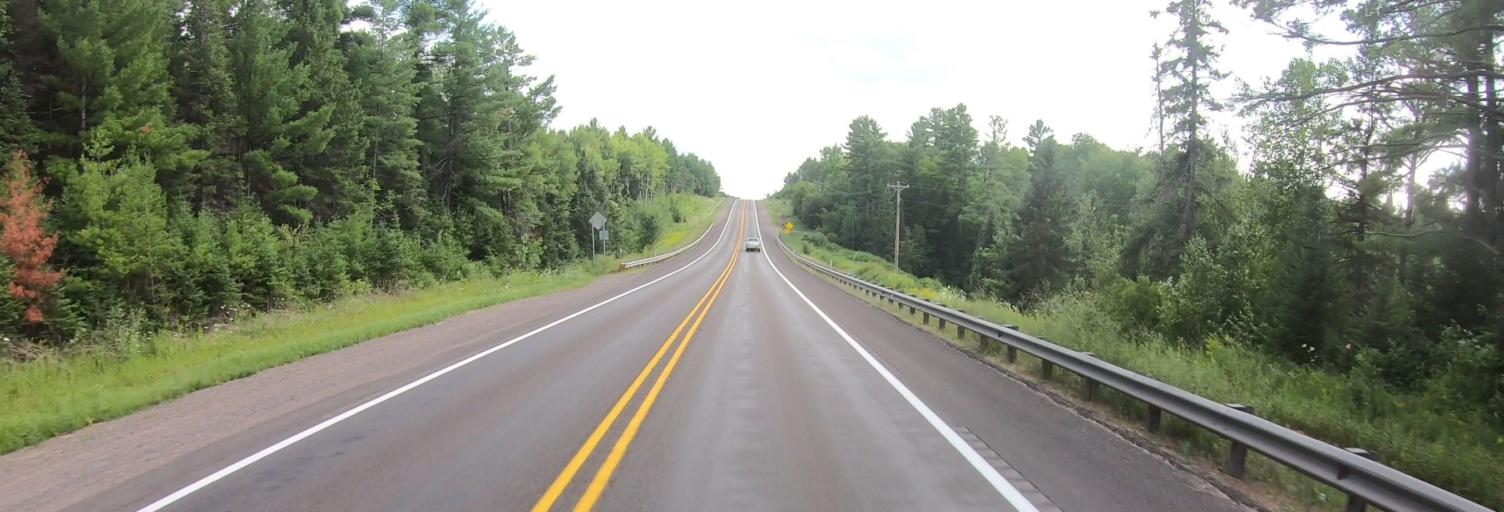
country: US
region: Michigan
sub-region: Ontonagon County
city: Ontonagon
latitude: 46.5570
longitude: -89.1786
